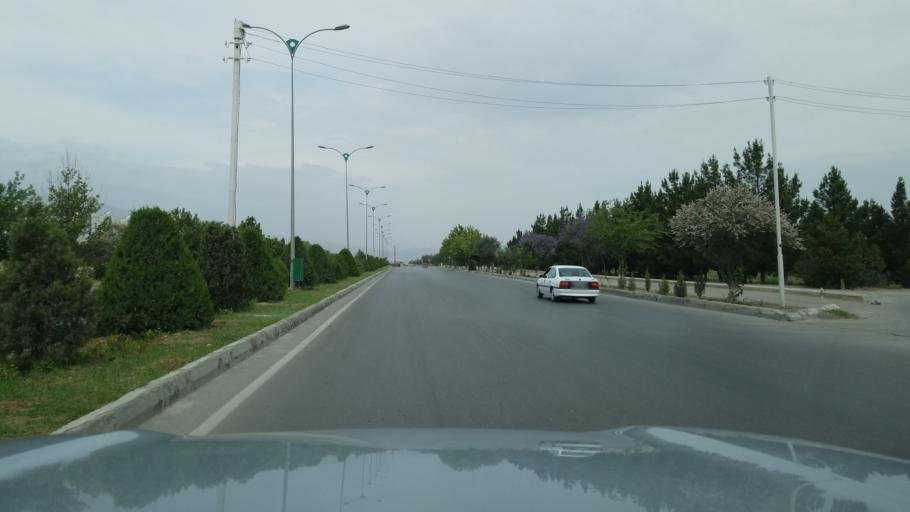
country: TM
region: Ahal
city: Abadan
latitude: 38.1647
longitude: 57.9390
